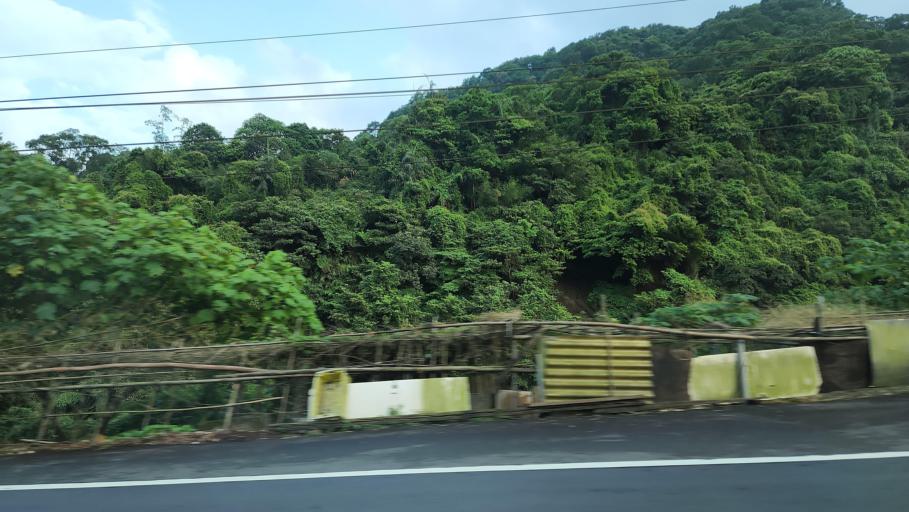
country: TW
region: Taiwan
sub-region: Keelung
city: Keelung
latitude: 25.1649
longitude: 121.6544
